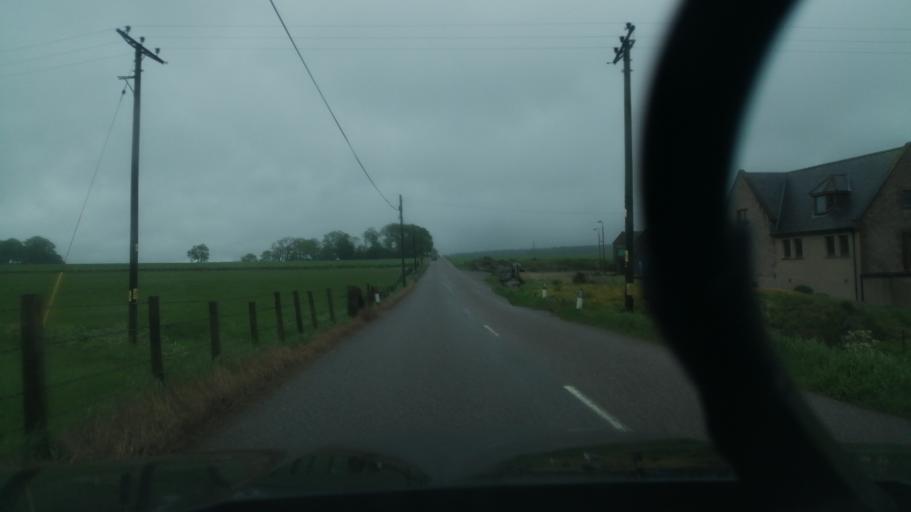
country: GB
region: Scotland
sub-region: Aberdeenshire
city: Huntly
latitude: 57.5479
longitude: -2.8201
